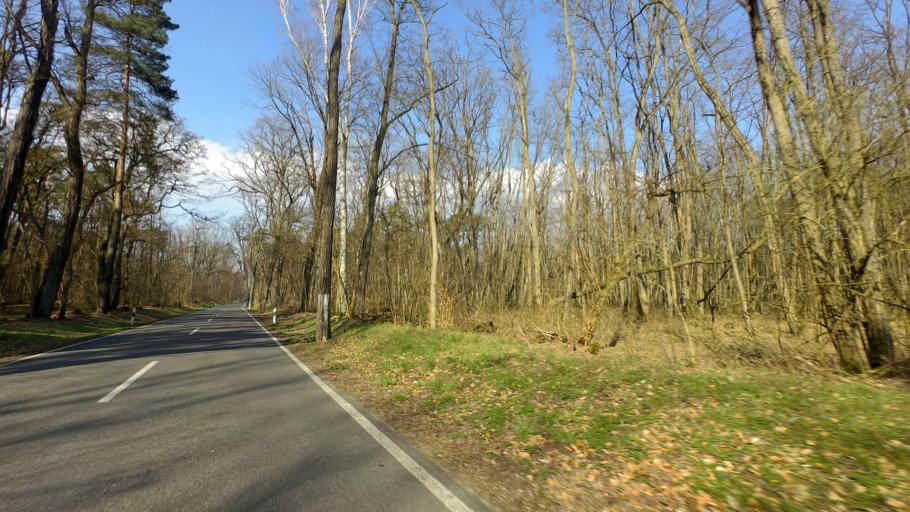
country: DE
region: Brandenburg
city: Dahme
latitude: 51.9116
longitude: 13.4843
